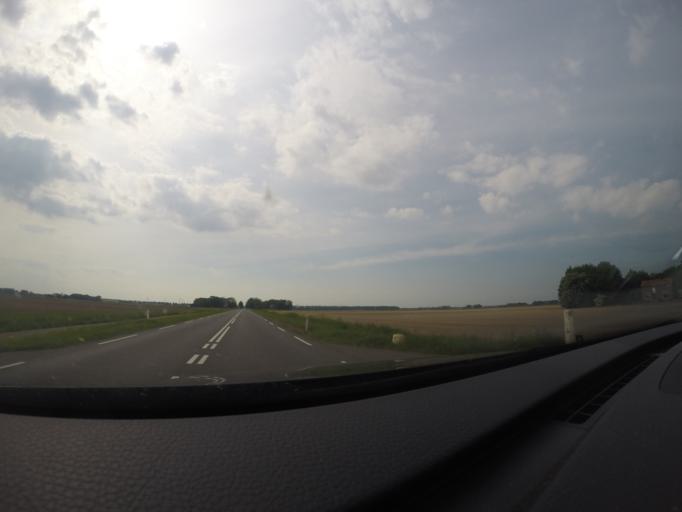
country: NL
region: Flevoland
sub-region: Gemeente Noordoostpolder
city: Ens
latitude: 52.6391
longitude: 5.7633
